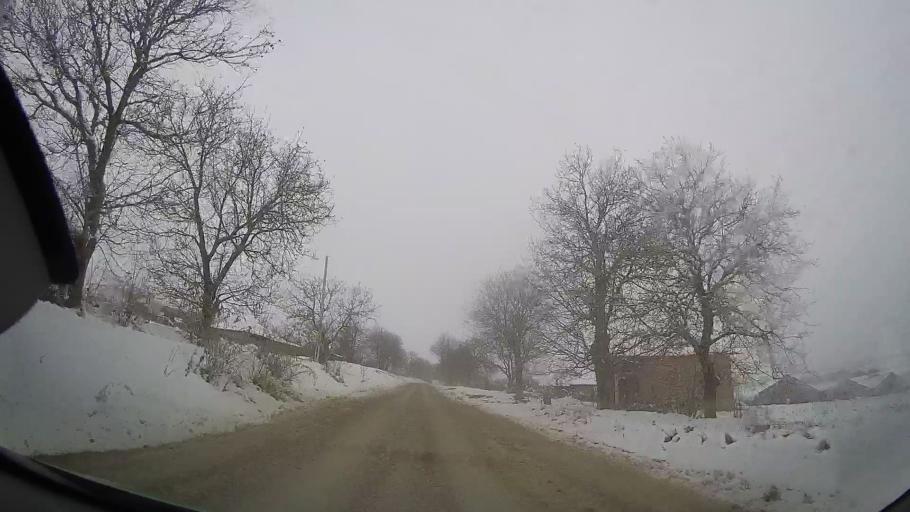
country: RO
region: Vaslui
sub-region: Comuna Todiresti
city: Todiresti
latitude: 46.8738
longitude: 27.3792
